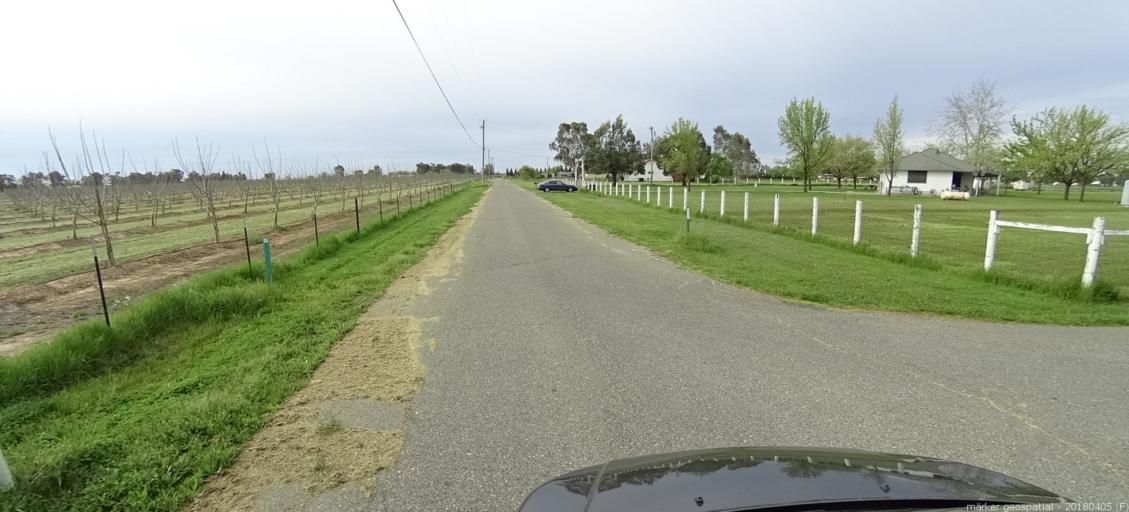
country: US
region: California
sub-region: Sacramento County
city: Herald
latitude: 38.2983
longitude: -121.2553
